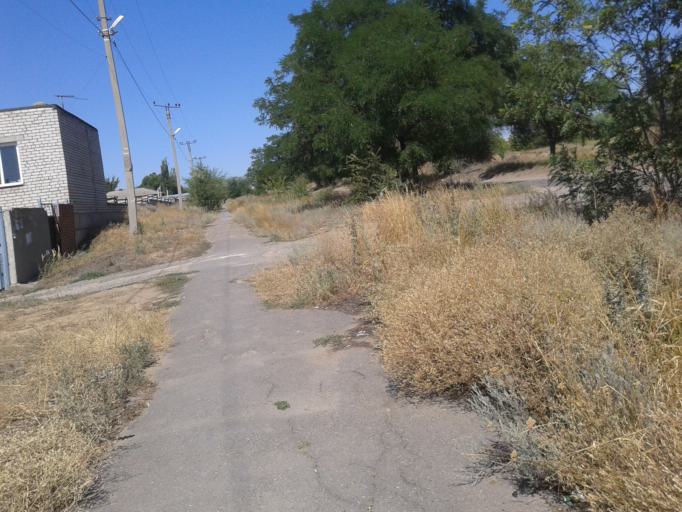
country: RU
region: Volgograd
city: Volgograd
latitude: 48.6895
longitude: 44.4491
